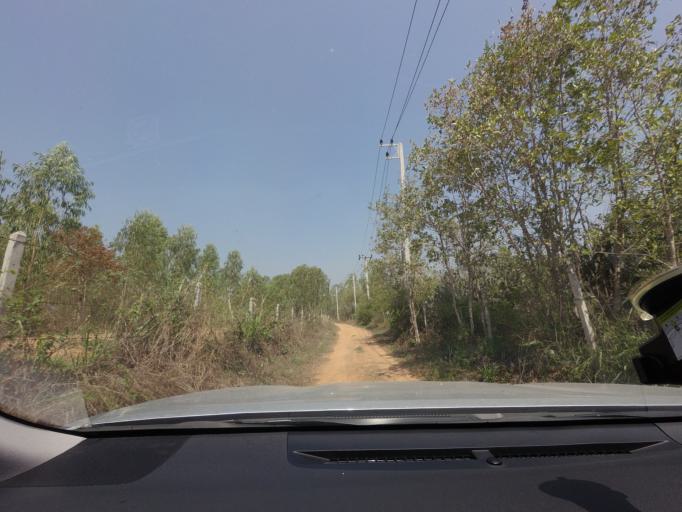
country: TH
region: Prachuap Khiri Khan
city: Prachuap Khiri Khan
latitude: 11.9322
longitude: 99.8184
